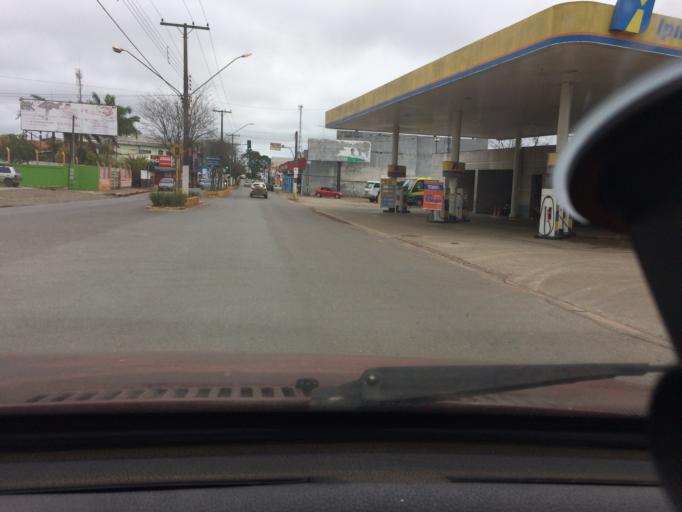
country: BR
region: Sao Paulo
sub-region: Capao Bonito
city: Capao Bonito
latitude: -24.0074
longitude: -48.3423
